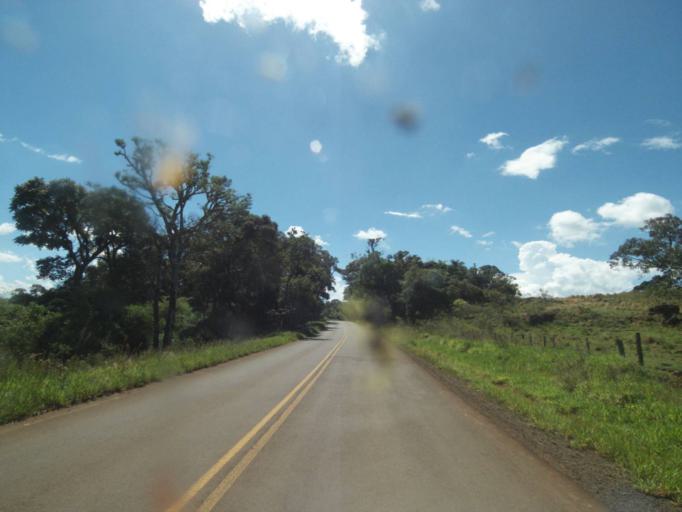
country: BR
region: Parana
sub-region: Pinhao
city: Pinhao
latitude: -25.7955
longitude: -52.0761
